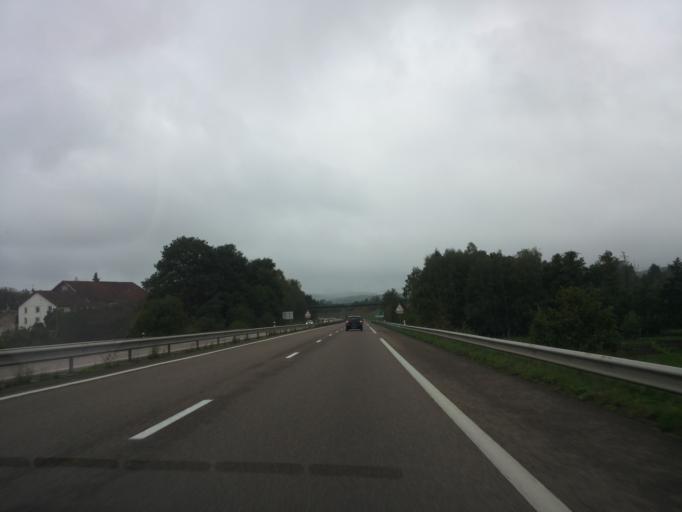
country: FR
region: Lorraine
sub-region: Departement des Vosges
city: Pouxeux
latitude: 48.1127
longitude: 6.5625
